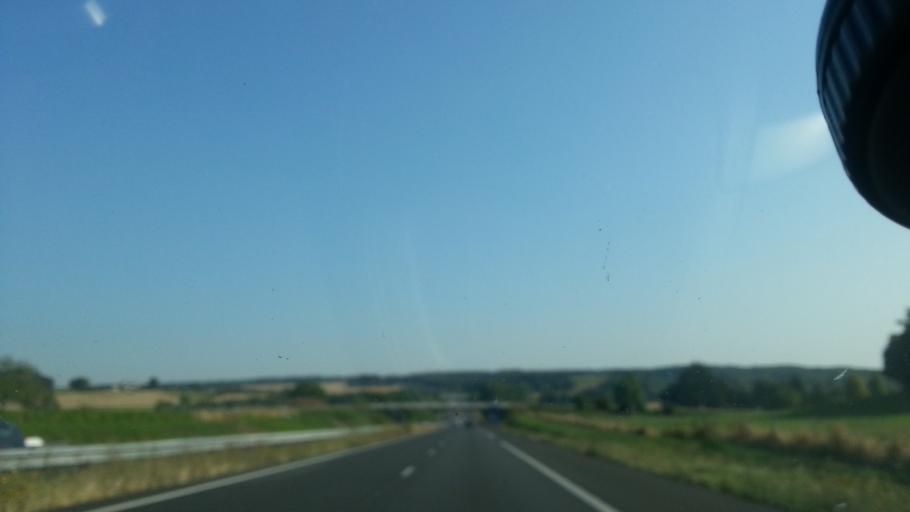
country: FR
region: Poitou-Charentes
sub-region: Departement de la Vienne
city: Dange-Saint-Romain
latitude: 46.9408
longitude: 0.5459
